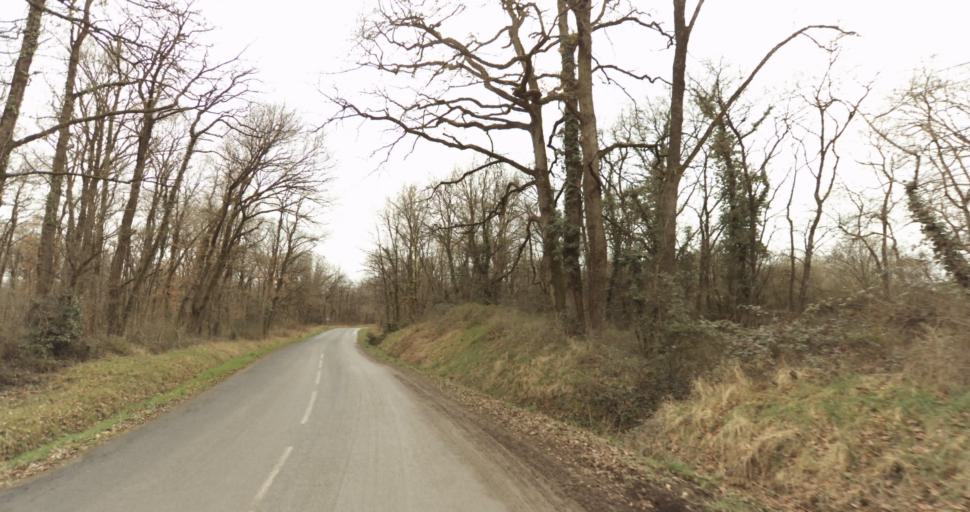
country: FR
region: Pays de la Loire
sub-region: Departement de Maine-et-Loire
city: Distre
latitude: 47.2543
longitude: -0.1145
